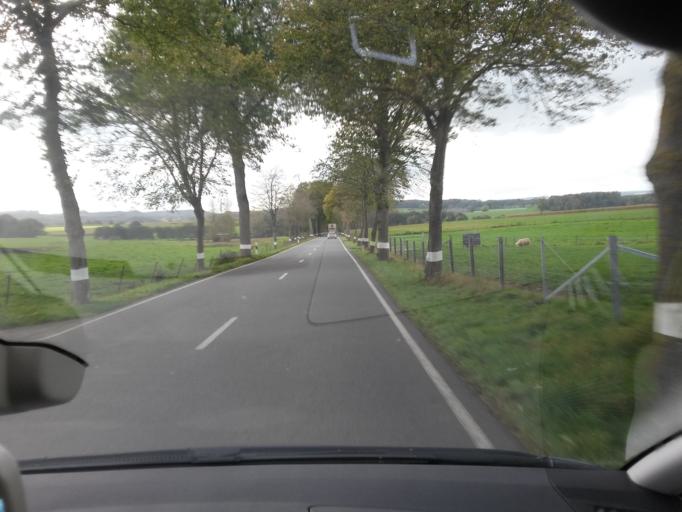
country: LU
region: Diekirch
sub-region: Canton de Redange
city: Beckerich
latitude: 49.7320
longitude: 5.8648
